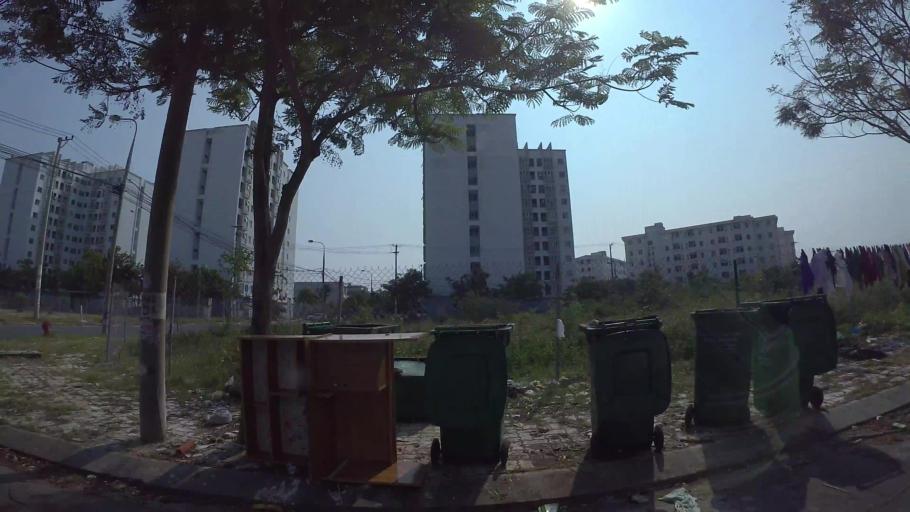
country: VN
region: Da Nang
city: Cam Le
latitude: 16.0073
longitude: 108.1970
